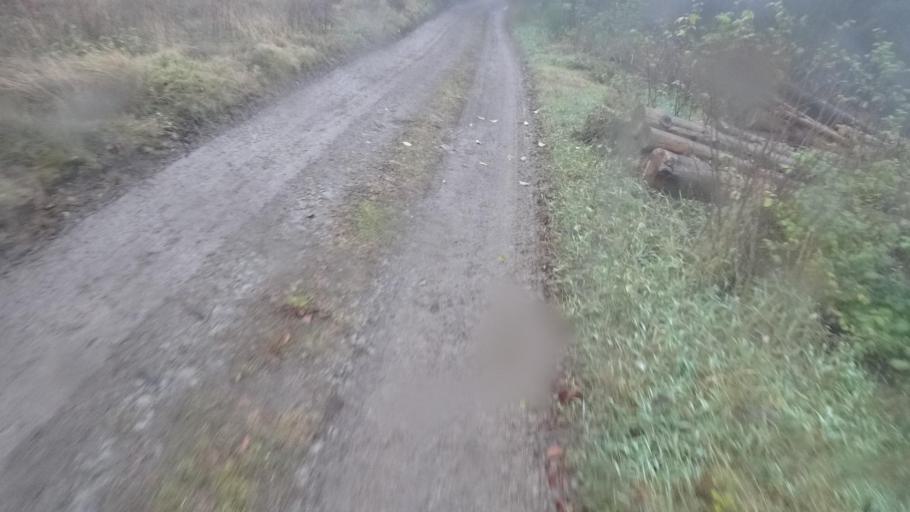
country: DE
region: Rheinland-Pfalz
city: Karbach
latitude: 50.1693
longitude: 7.6030
